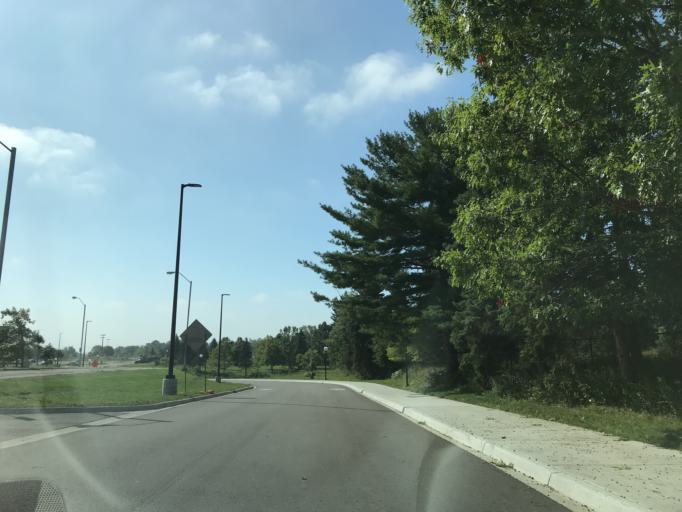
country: US
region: Michigan
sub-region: Washtenaw County
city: Ann Arbor
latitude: 42.2992
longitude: -83.7089
